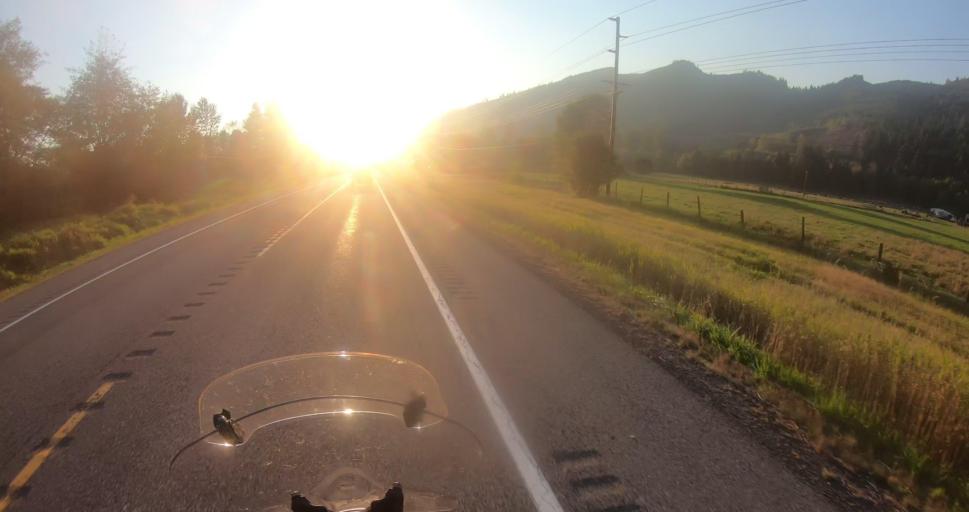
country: US
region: Washington
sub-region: Lewis County
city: Morton
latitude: 46.5381
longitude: -122.1086
